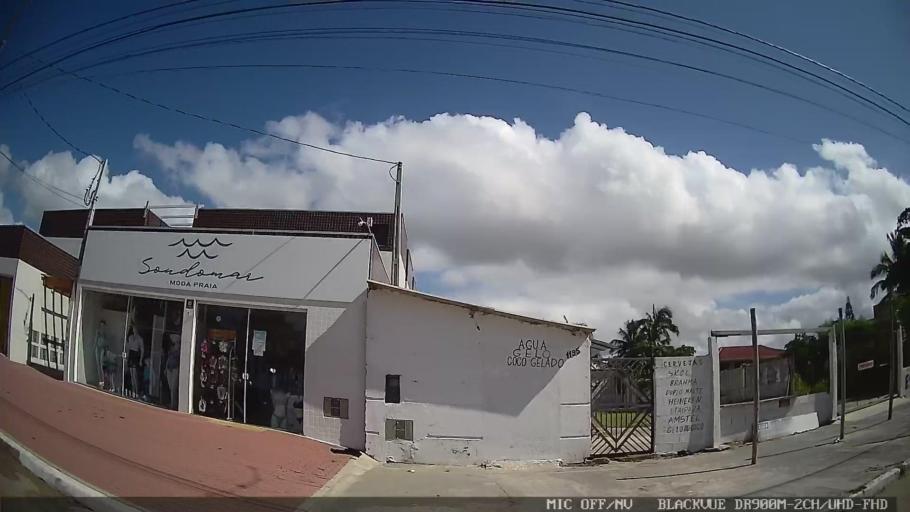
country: BR
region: Sao Paulo
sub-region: Peruibe
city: Peruibe
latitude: -24.3234
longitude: -46.9942
